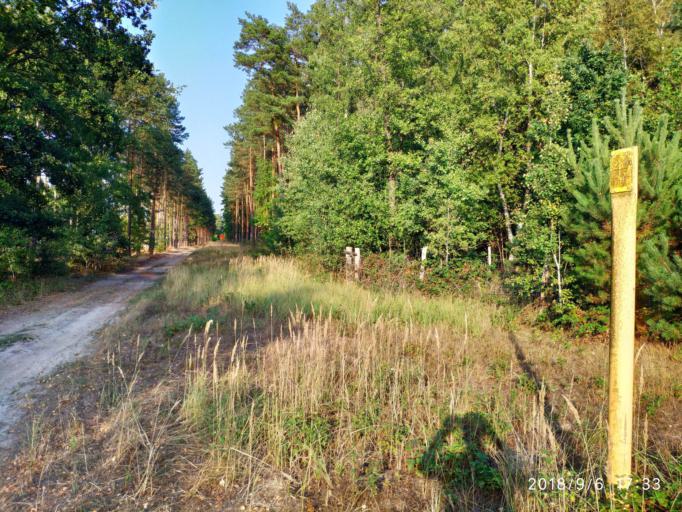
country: PL
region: Lubusz
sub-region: Powiat zielonogorski
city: Swidnica
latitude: 51.9203
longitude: 15.3707
